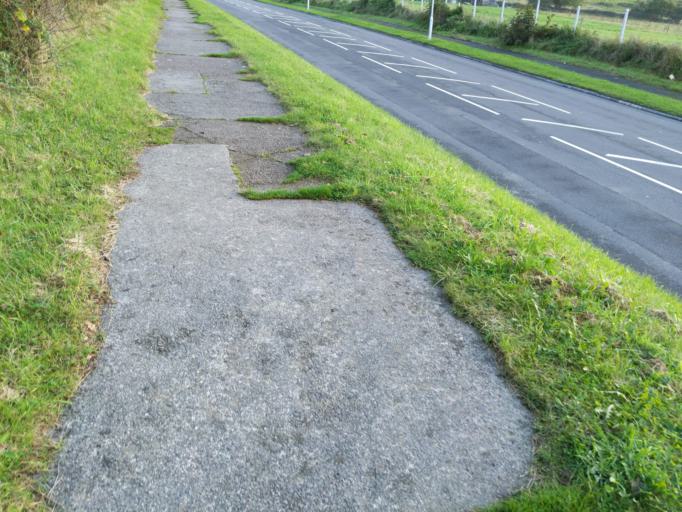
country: GB
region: England
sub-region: Cornwall
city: Saltash
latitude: 50.4158
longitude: -4.1858
